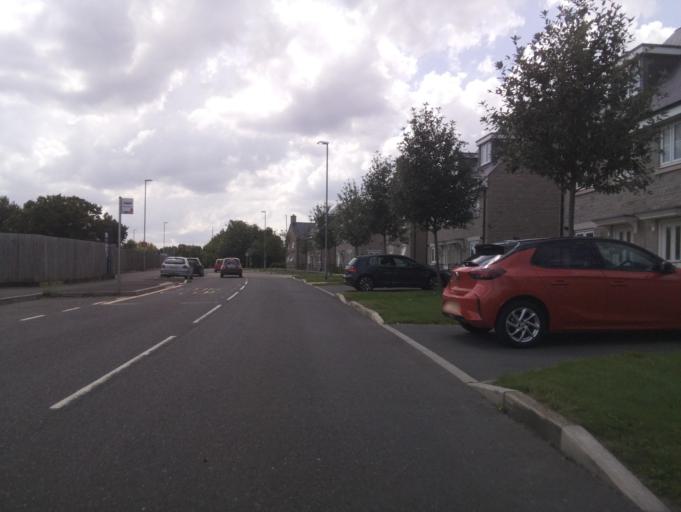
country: GB
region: England
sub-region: Wiltshire
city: Purton
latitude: 51.5810
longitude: -1.8383
